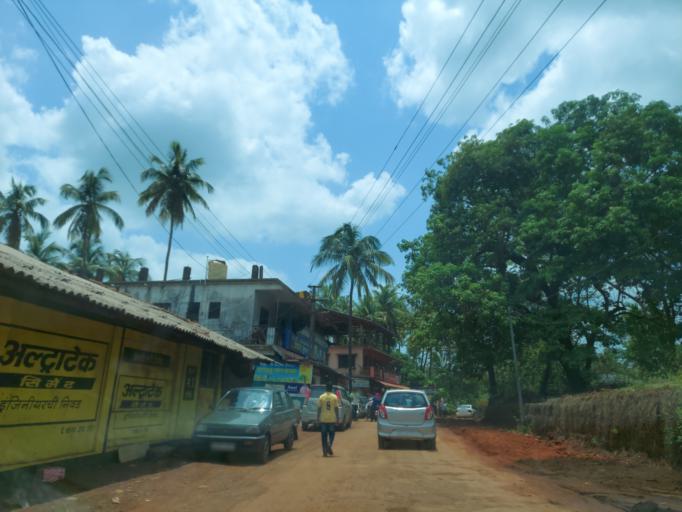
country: IN
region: Maharashtra
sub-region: Sindhudurg
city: Savantvadi
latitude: 15.8181
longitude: 73.8659
